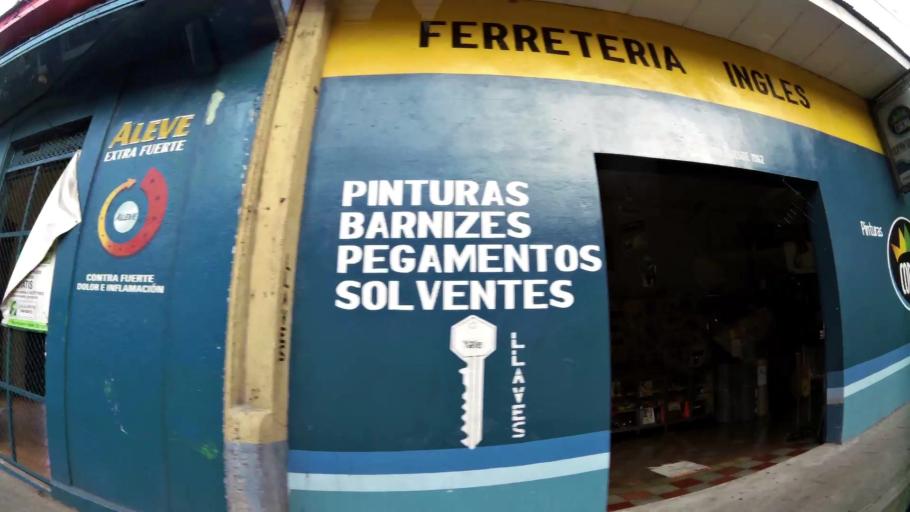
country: SV
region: San Vicente
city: San Vicente
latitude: 13.6438
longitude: -88.7850
